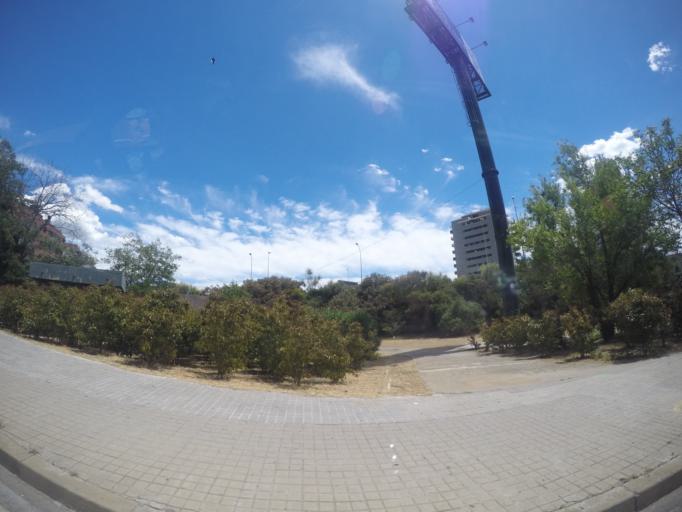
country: ES
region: Catalonia
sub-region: Provincia de Barcelona
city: Badalona
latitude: 41.4572
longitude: 2.2483
